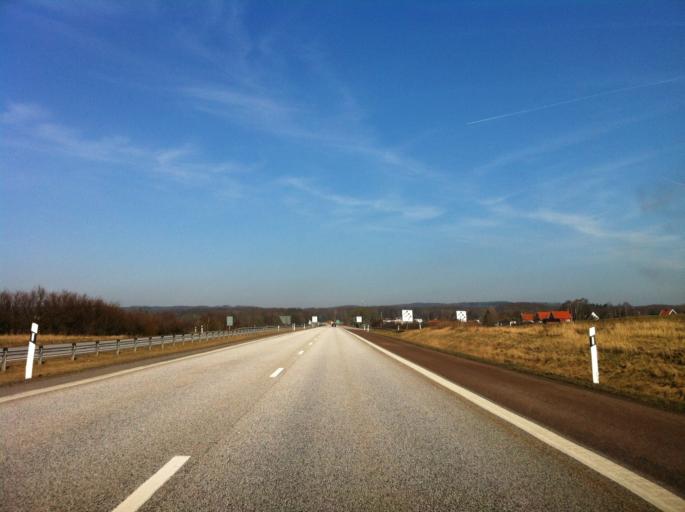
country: SE
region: Skane
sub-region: Angelholms Kommun
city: Munka-Ljungby
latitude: 56.3137
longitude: 12.9116
